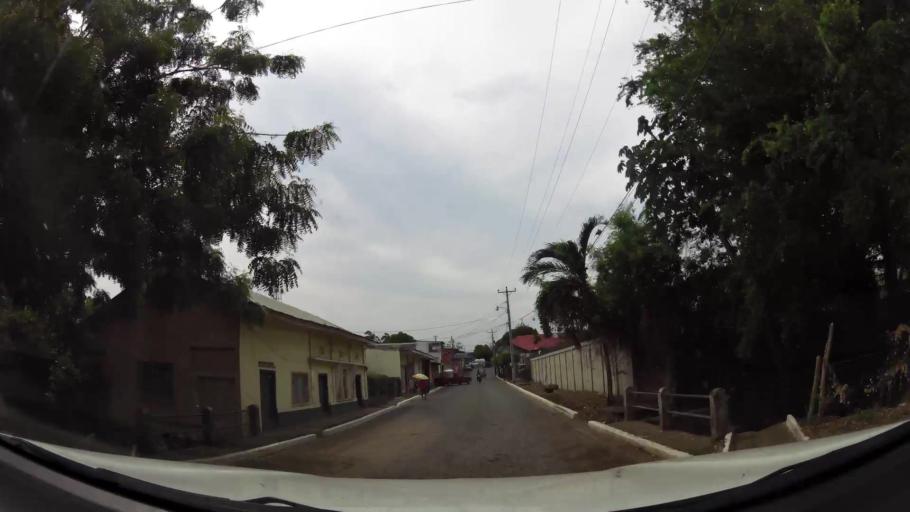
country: NI
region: Rivas
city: Rivas
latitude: 11.4371
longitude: -85.8278
